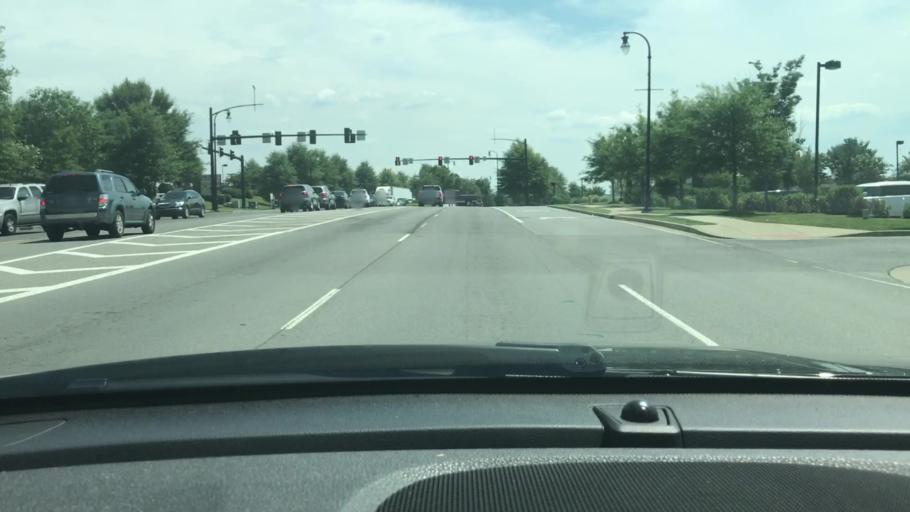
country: US
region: Tennessee
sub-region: Sumner County
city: Hendersonville
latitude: 36.3304
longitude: -86.5937
